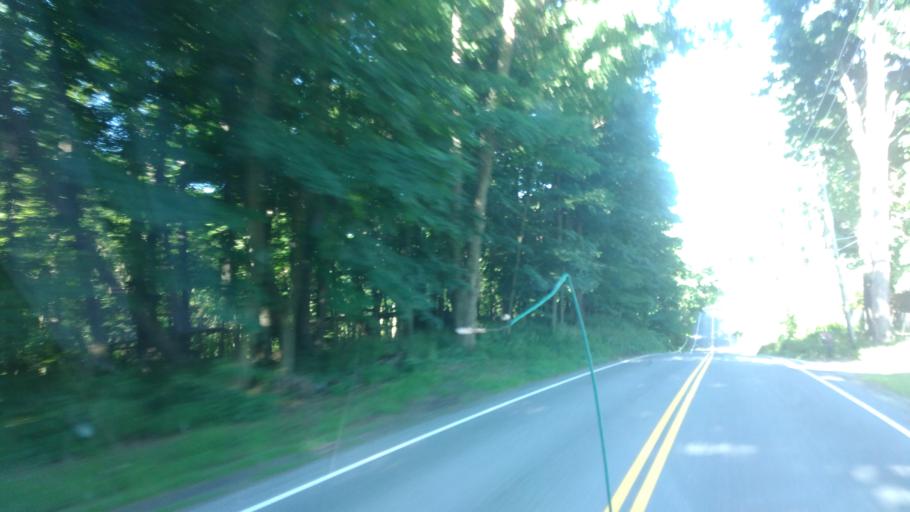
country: US
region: New York
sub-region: Monroe County
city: Webster
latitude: 43.2578
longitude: -77.4614
